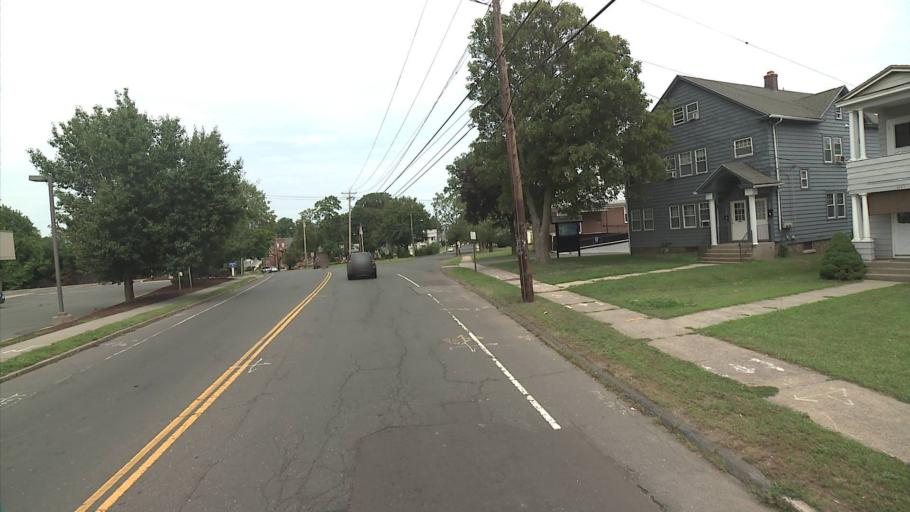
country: US
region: Connecticut
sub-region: Hartford County
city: New Britain
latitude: 41.6837
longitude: -72.7675
